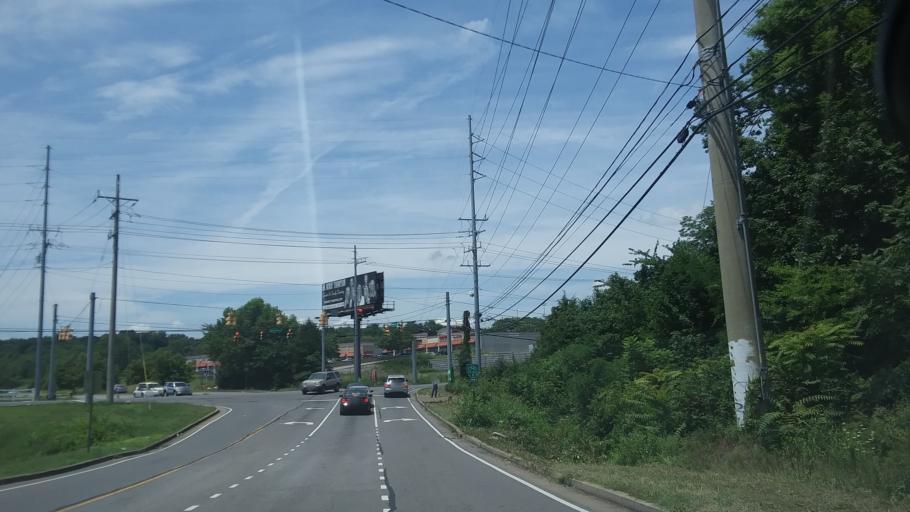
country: US
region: Tennessee
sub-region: Rutherford County
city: La Vergne
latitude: 36.0651
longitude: -86.6276
